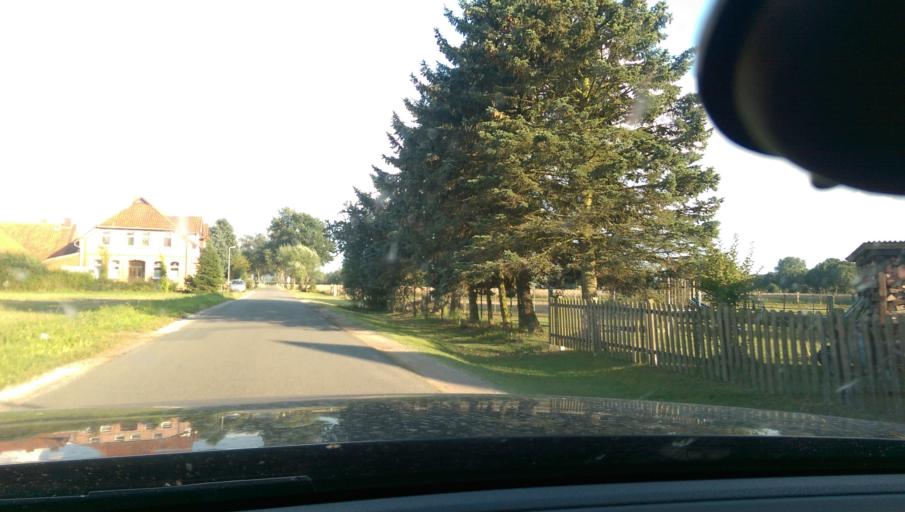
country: DE
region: Lower Saxony
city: Lindwedel
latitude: 52.6000
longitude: 9.6128
